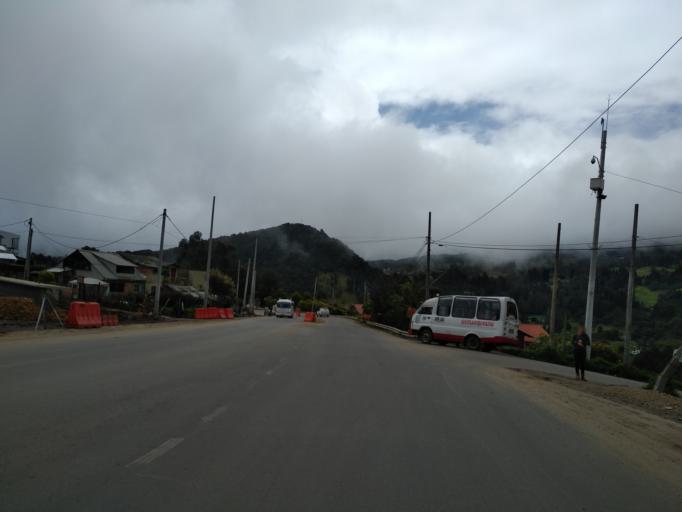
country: CO
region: Bogota D.C.
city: Barrio San Luis
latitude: 4.6601
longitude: -74.0066
